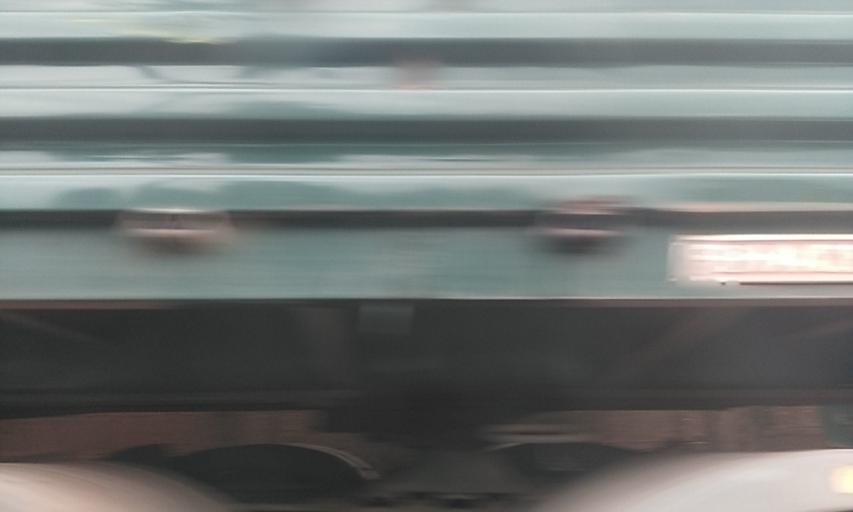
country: UG
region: Central Region
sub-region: Wakiso District
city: Bweyogerere
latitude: 0.3618
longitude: 32.6661
